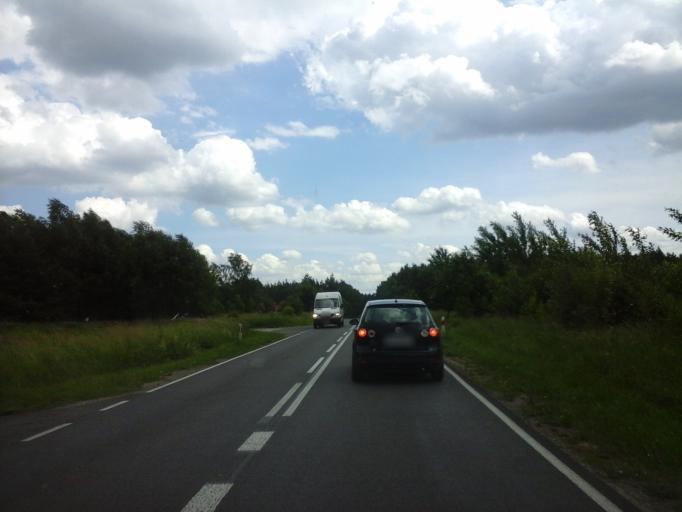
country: PL
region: West Pomeranian Voivodeship
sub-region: Powiat swidwinski
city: Slawoborze
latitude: 53.8824
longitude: 15.7221
